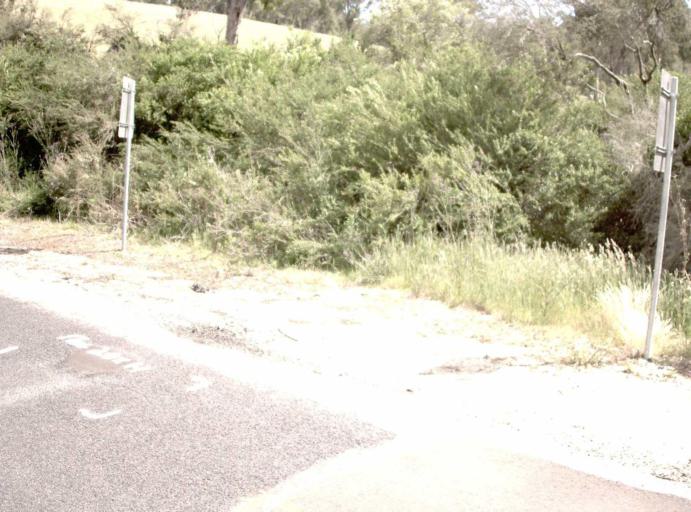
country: AU
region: New South Wales
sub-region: Bega Valley
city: Eden
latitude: -37.4805
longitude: 149.5989
